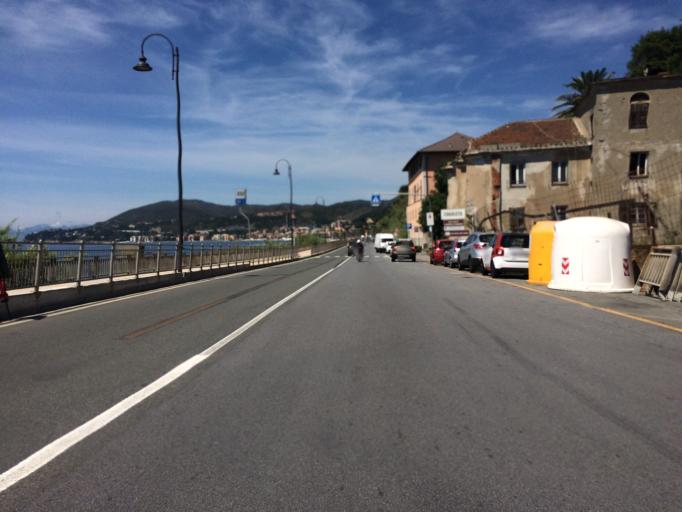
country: IT
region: Liguria
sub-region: Provincia di Genova
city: Cogoleto
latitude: 44.3910
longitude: 8.6638
